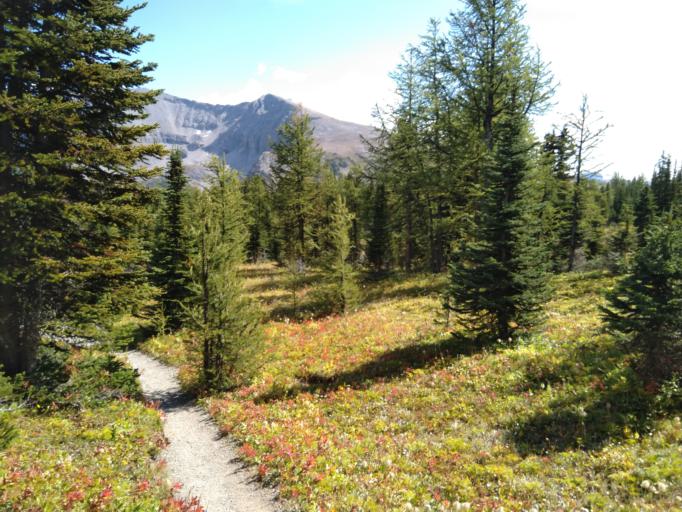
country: CA
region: Alberta
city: Banff
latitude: 51.0845
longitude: -115.7878
